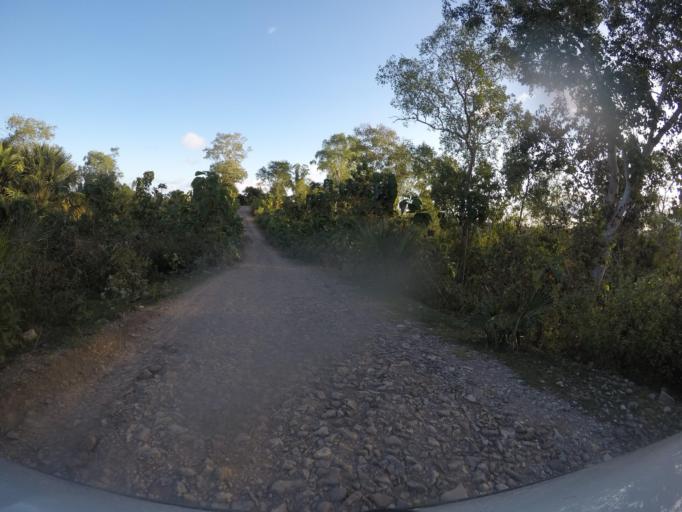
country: TL
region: Baucau
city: Venilale
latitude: -8.7179
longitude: 126.7123
